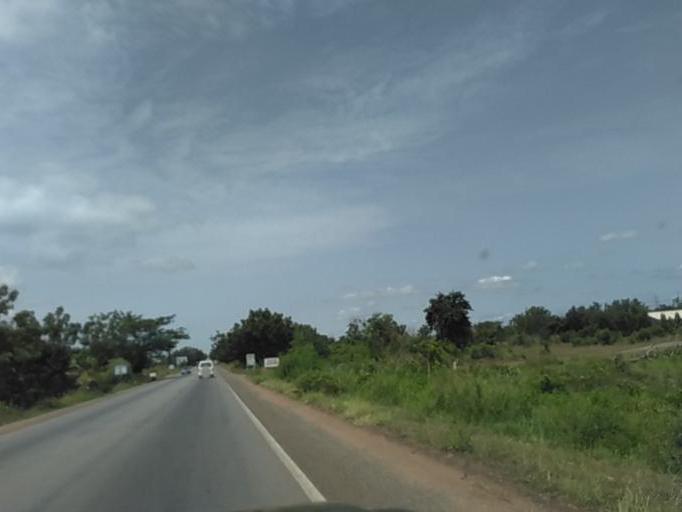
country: GH
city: Akropong
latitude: 6.1027
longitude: 0.0464
